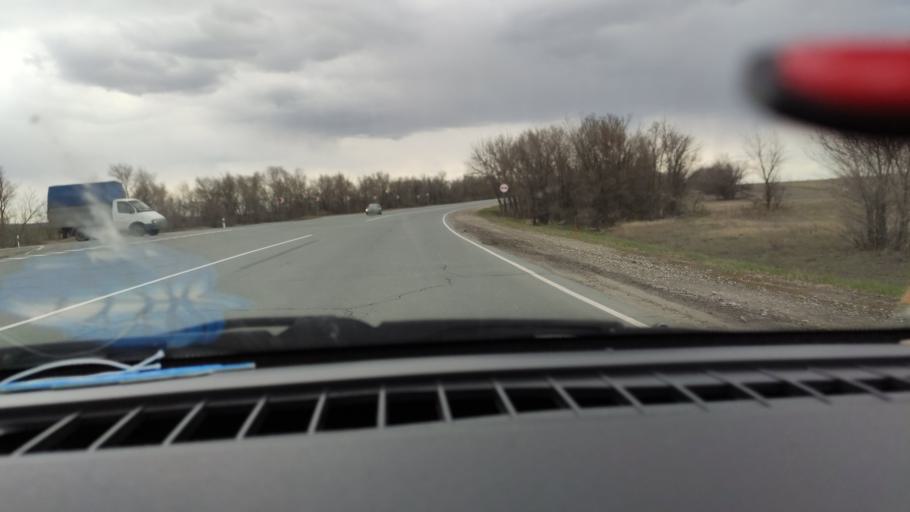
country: RU
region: Saratov
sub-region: Saratovskiy Rayon
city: Saratov
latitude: 51.7128
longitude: 46.0216
